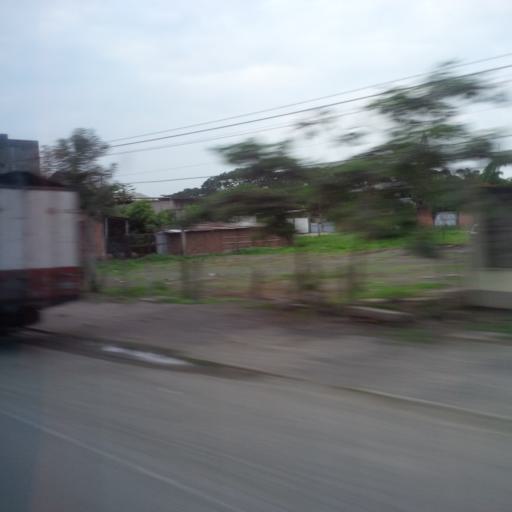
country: EC
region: Canar
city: La Troncal
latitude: -2.3354
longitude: -79.3957
